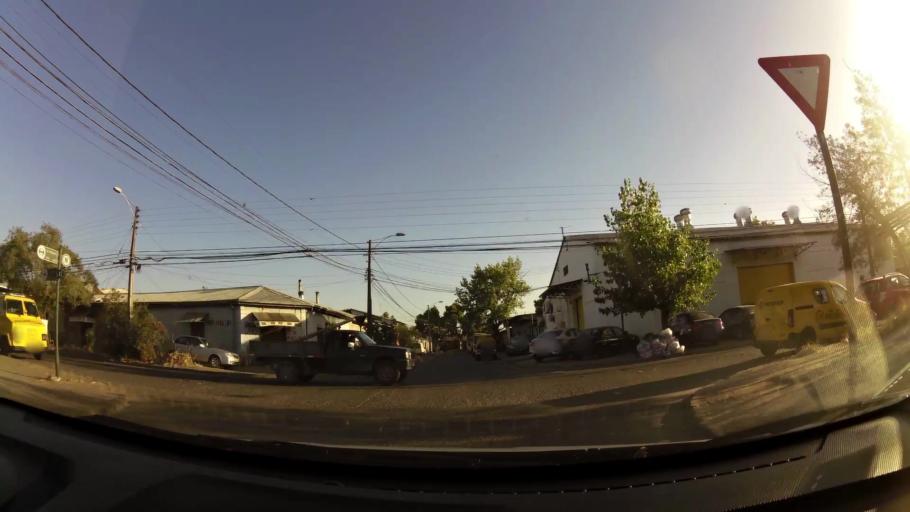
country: CL
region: Maule
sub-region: Provincia de Talca
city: Talca
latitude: -35.4329
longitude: -71.6434
